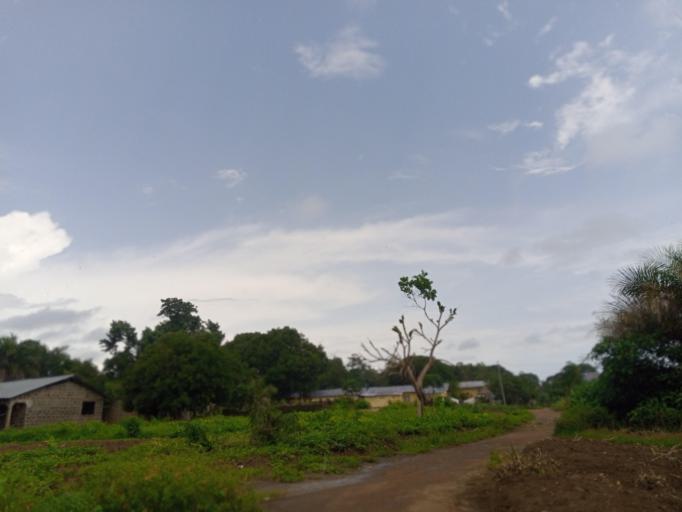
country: SL
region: Northern Province
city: Sawkta
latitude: 8.6324
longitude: -13.2046
